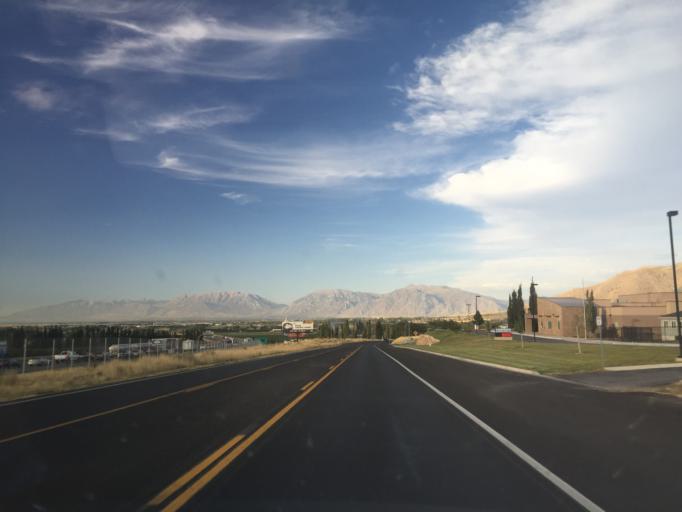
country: US
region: Utah
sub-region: Utah County
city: Santaquin
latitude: 39.9813
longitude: -111.7670
